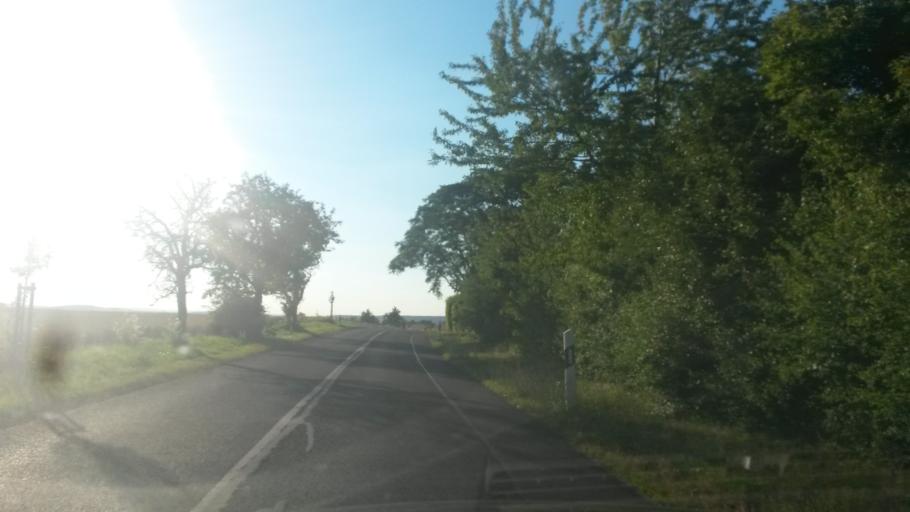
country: DE
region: Bavaria
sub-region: Regierungsbezirk Unterfranken
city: Wuerzburg
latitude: 49.8134
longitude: 9.9405
